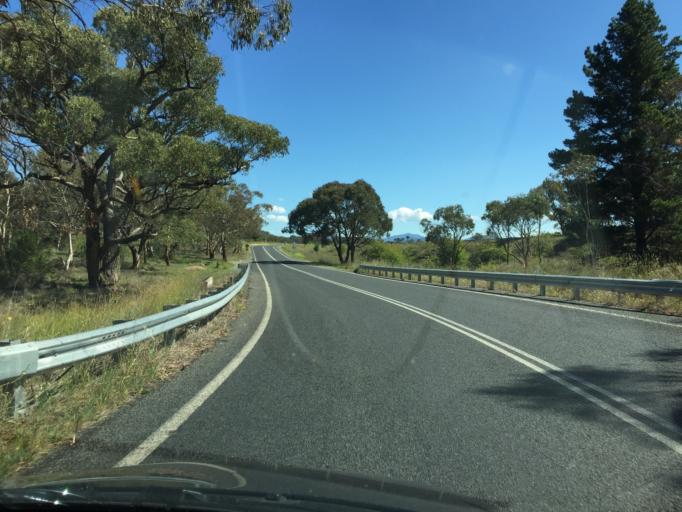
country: AU
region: Australian Capital Territory
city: Macarthur
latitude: -35.4975
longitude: 149.1524
